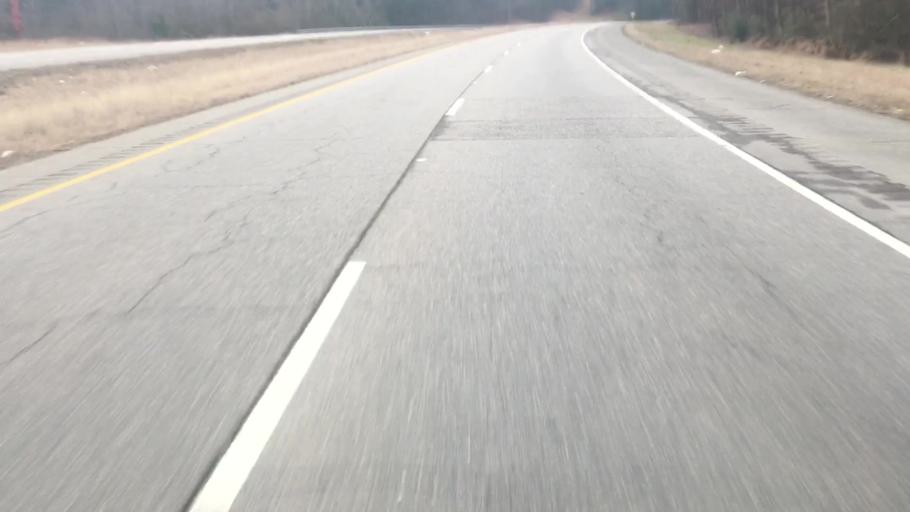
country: US
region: Alabama
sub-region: Walker County
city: Sumiton
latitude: 33.7736
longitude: -87.0745
